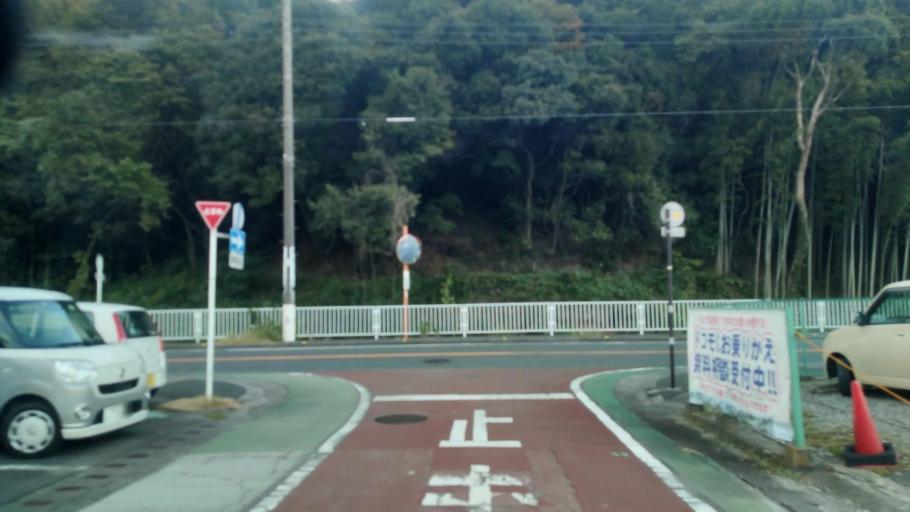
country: JP
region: Shizuoka
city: Ito
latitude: 34.9591
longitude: 139.0911
